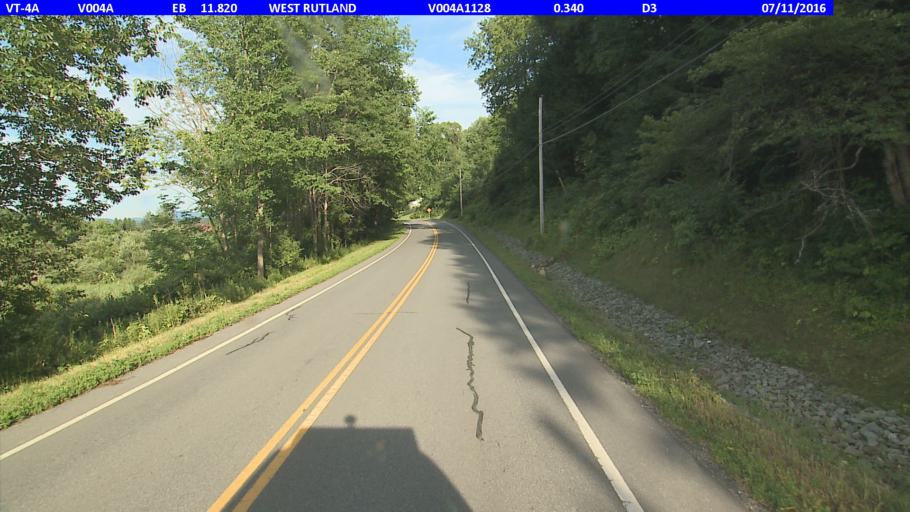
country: US
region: Vermont
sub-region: Rutland County
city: West Rutland
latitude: 43.6050
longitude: -73.0820
